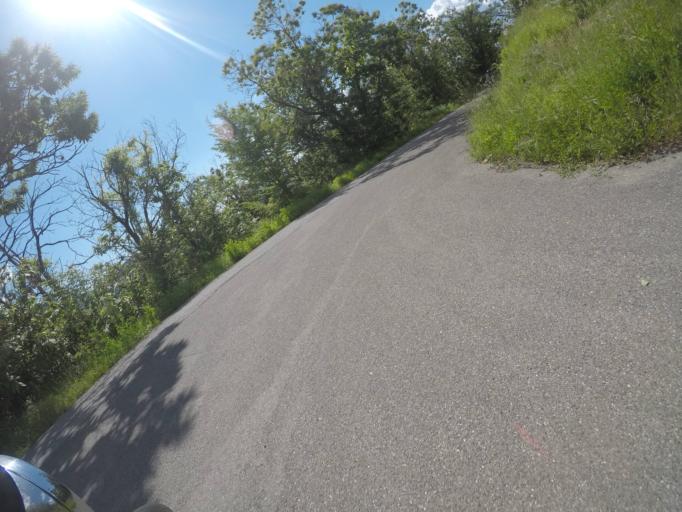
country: IT
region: Tuscany
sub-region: Provincia di Massa-Carrara
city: Casola in Lunigiana
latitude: 44.1760
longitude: 10.1655
